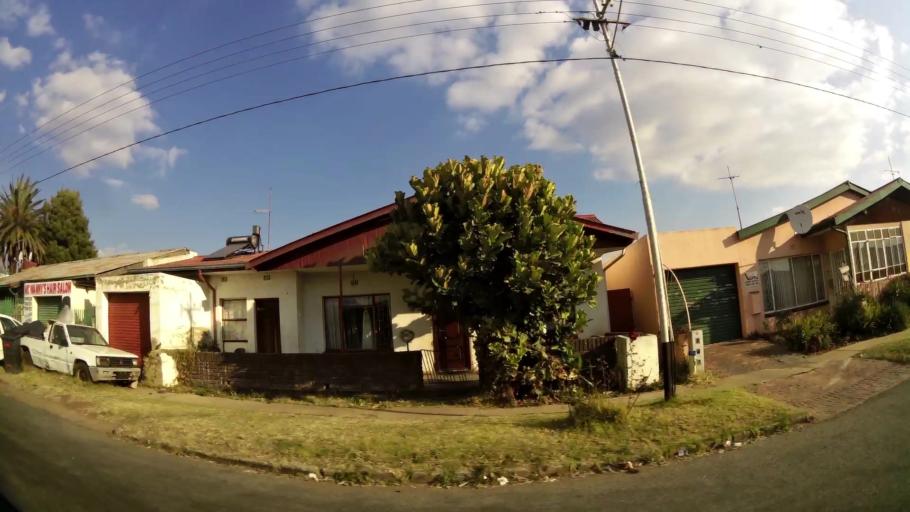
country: ZA
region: Gauteng
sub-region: West Rand District Municipality
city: Krugersdorp
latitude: -26.0982
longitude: 27.7589
